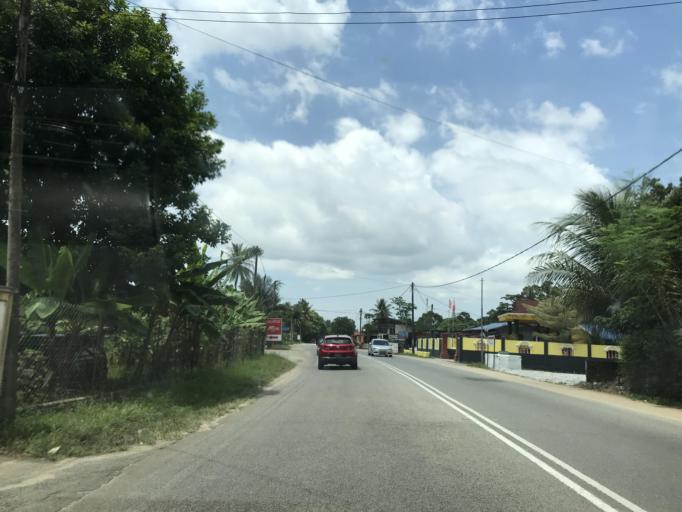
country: MY
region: Kelantan
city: Pasir Mas
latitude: 6.0538
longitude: 102.1917
